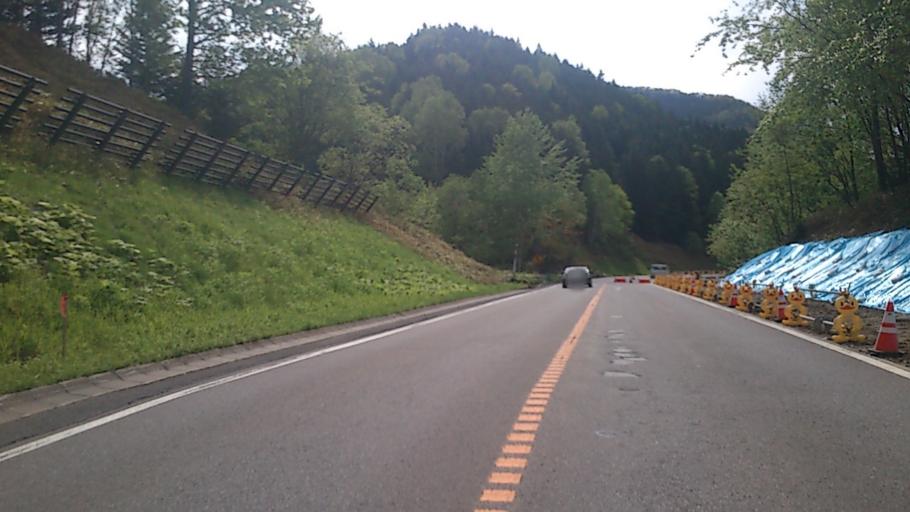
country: JP
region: Hokkaido
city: Kamikawa
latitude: 43.6853
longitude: 143.0303
